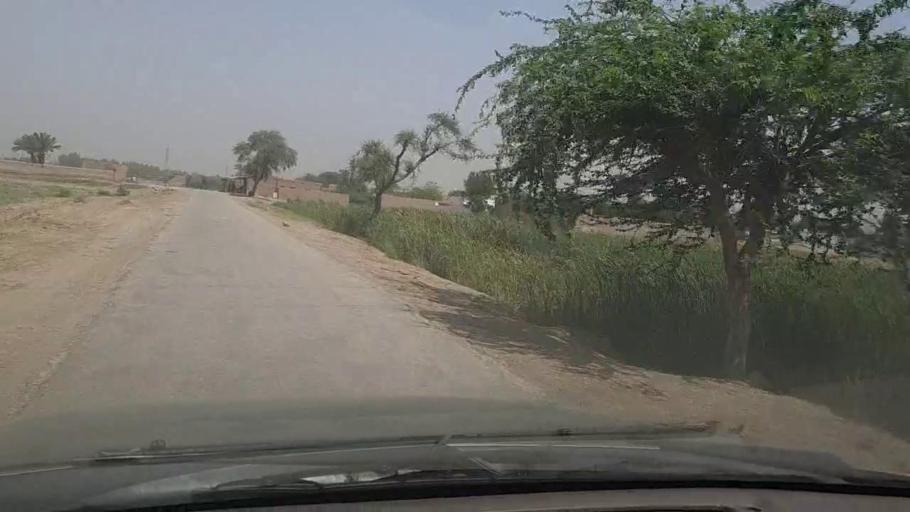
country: PK
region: Sindh
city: Madeji
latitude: 27.8243
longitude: 68.3950
